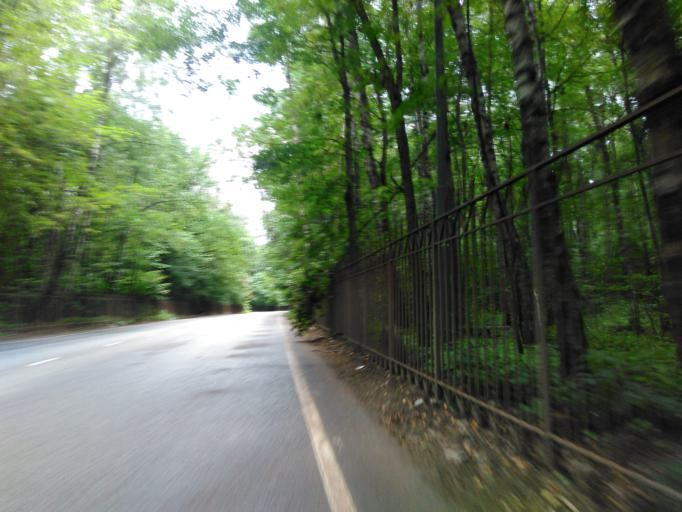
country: RU
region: Moscow
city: Rostokino
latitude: 55.8277
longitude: 37.6920
